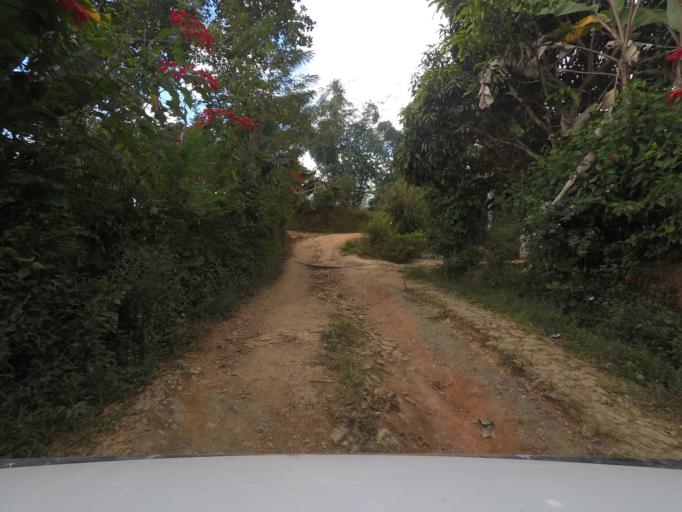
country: TL
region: Ermera
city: Gleno
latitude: -8.7214
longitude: 125.3241
